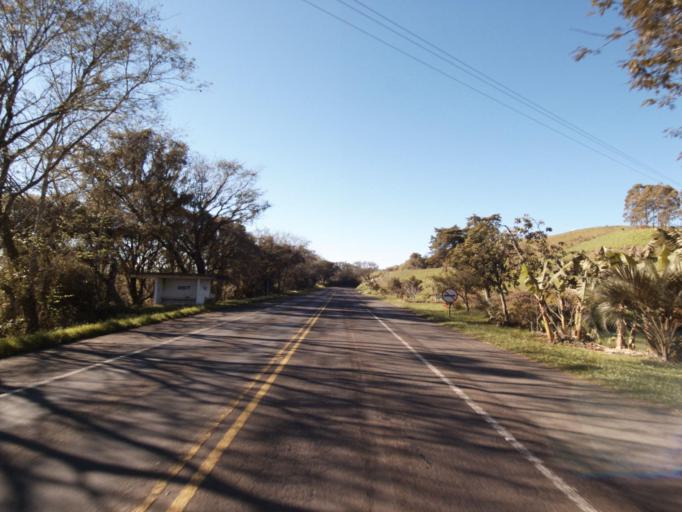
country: BR
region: Rio Grande do Sul
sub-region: Frederico Westphalen
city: Frederico Westphalen
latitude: -26.8036
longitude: -53.4444
